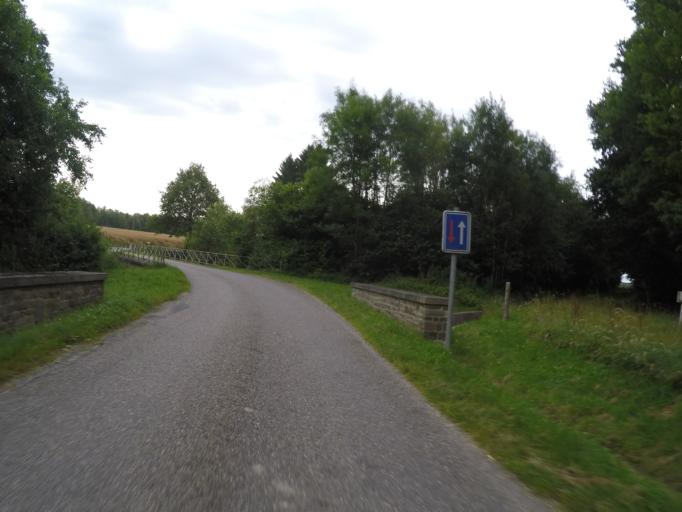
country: BE
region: Wallonia
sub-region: Province de Namur
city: Assesse
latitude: 50.3168
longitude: 5.0382
